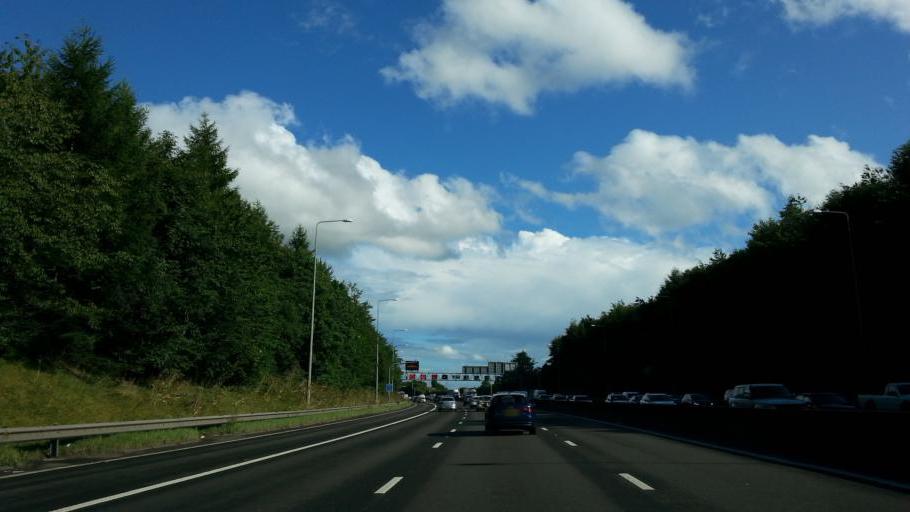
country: GB
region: England
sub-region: City and Borough of Leeds
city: Gildersome
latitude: 53.7399
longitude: -1.6239
